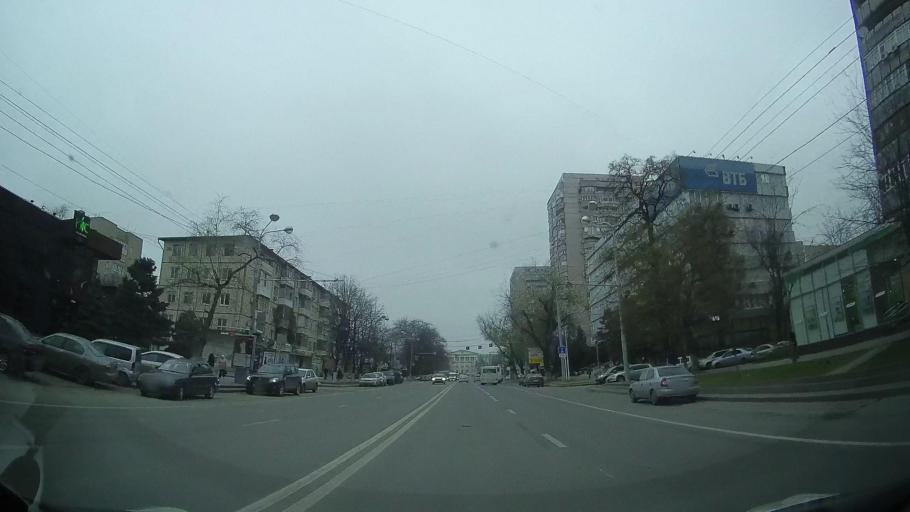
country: RU
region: Rostov
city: Rostov-na-Donu
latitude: 47.2322
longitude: 39.7145
